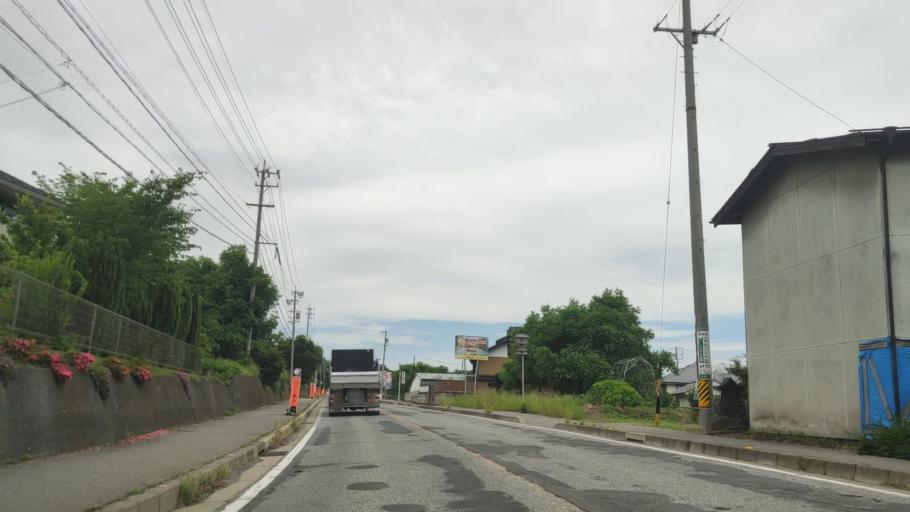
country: JP
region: Nagano
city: Komoro
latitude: 36.3452
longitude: 138.3758
